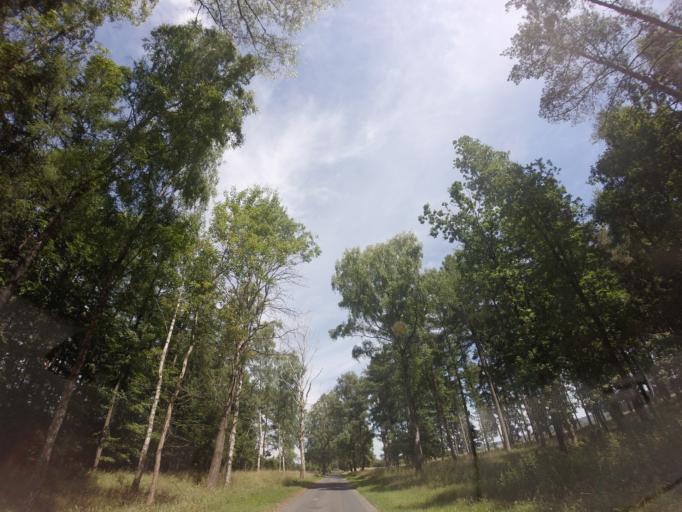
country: PL
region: West Pomeranian Voivodeship
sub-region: Powiat choszczenski
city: Recz
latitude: 53.3380
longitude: 15.5261
